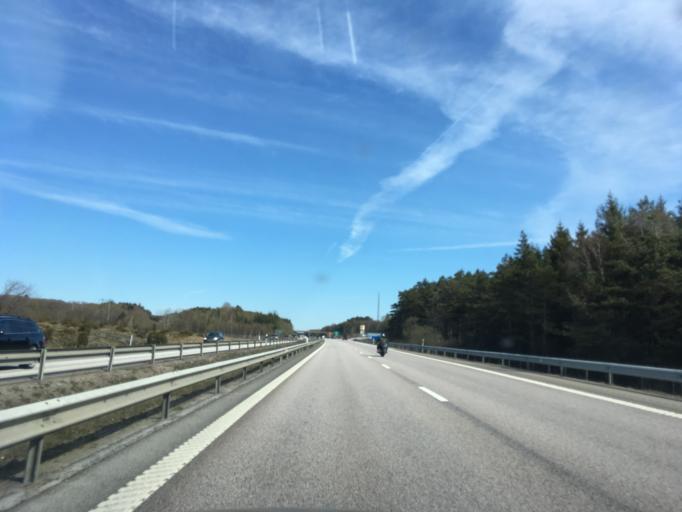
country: SE
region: Vaestra Goetaland
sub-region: Molndal
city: Lindome
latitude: 57.5451
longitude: 12.0527
